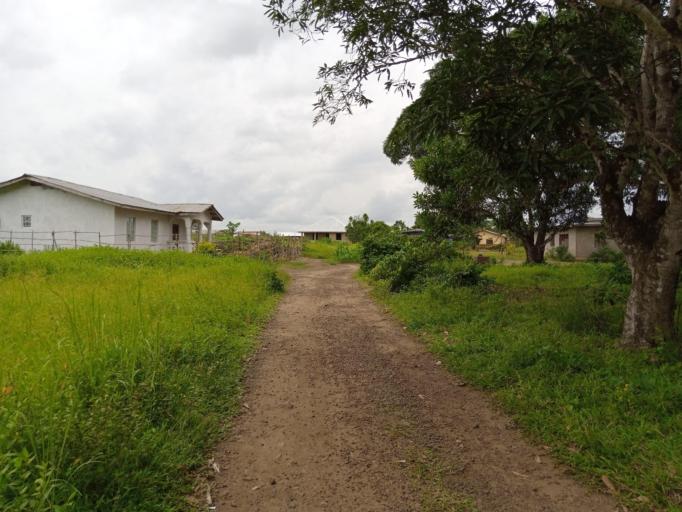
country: SL
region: Southern Province
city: Moyamba
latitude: 8.1618
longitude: -12.4249
